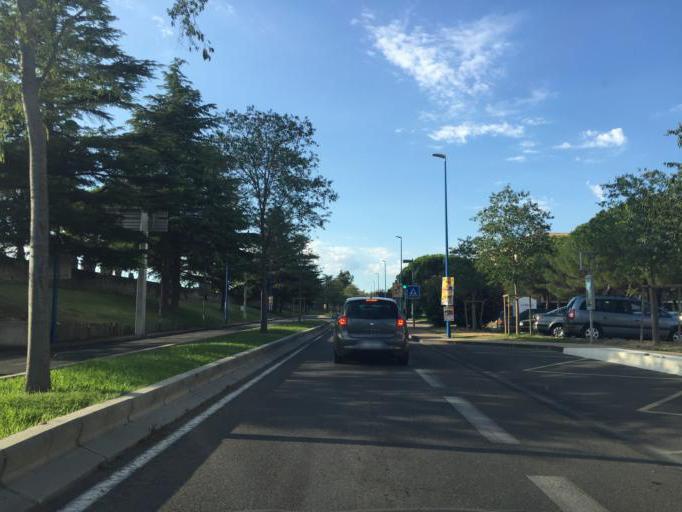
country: FR
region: Provence-Alpes-Cote d'Azur
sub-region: Departement du Vaucluse
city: Carpentras
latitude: 44.0422
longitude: 5.0489
